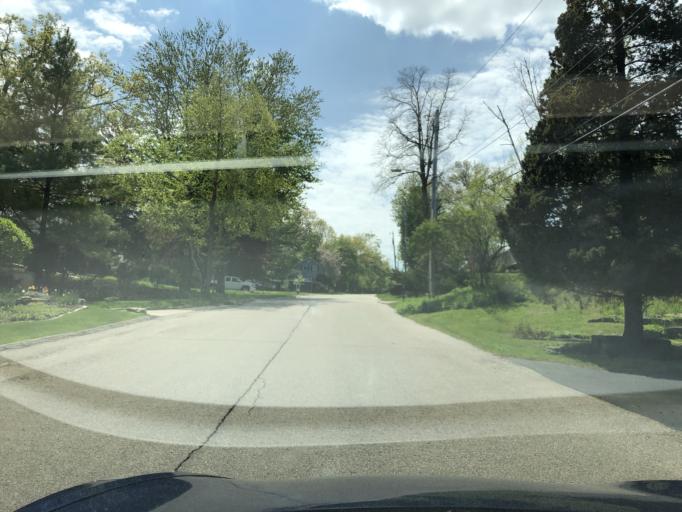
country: US
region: Iowa
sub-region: Dubuque County
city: Dubuque
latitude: 42.4813
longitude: -90.6615
